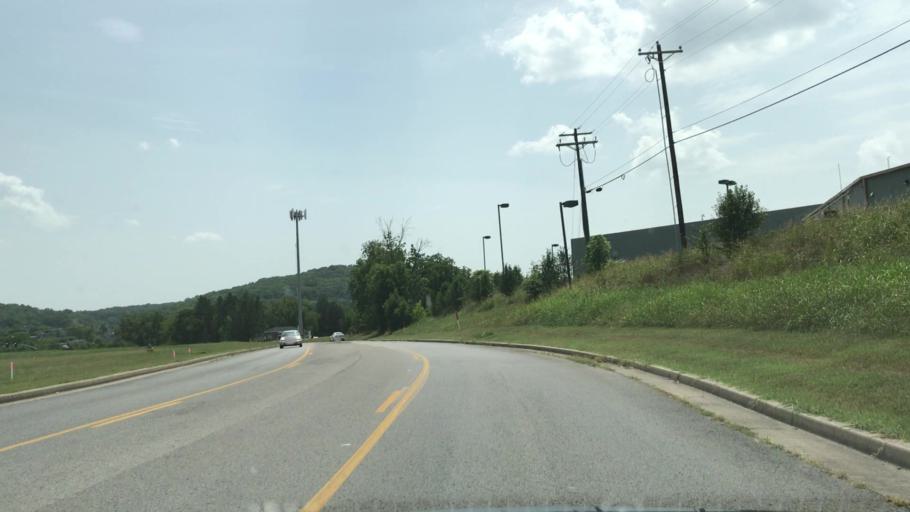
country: US
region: Tennessee
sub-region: Rutherford County
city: Smyrna
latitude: 35.9808
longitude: -86.5539
